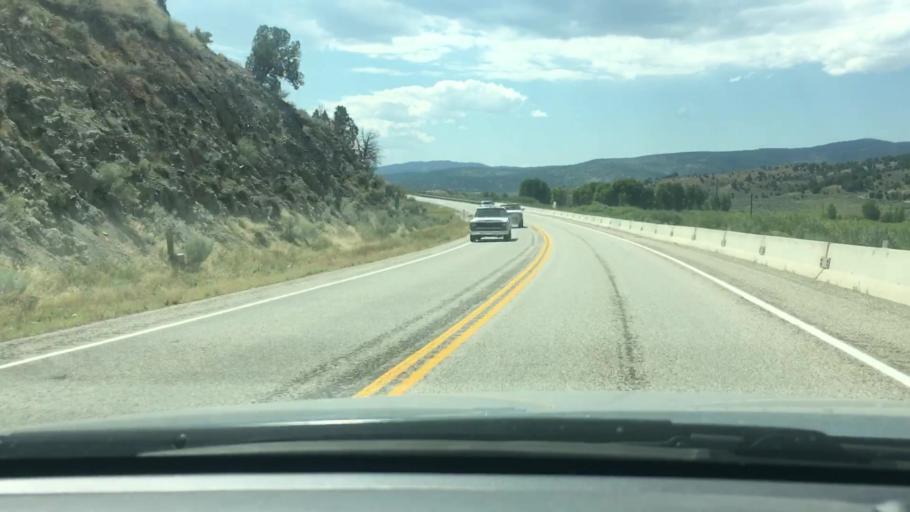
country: US
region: Utah
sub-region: Utah County
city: Woodland Hills
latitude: 39.9472
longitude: -111.5382
